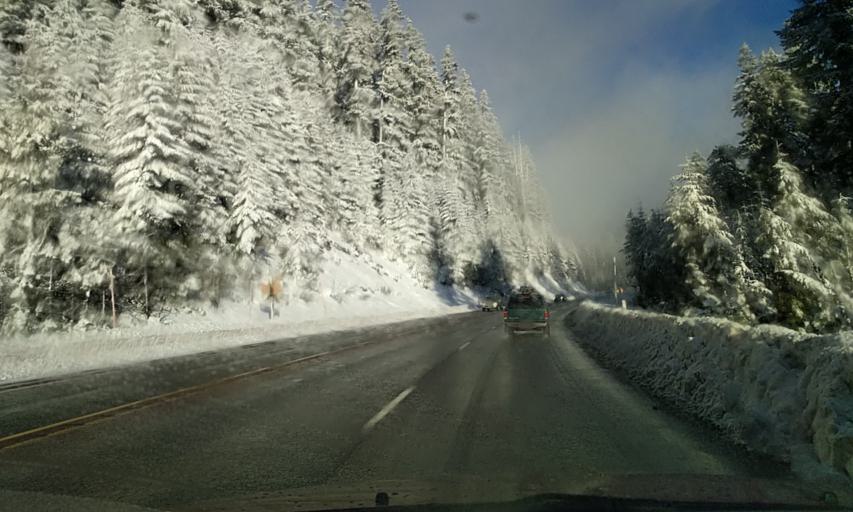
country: US
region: Oregon
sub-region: Clackamas County
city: Mount Hood Village
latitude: 45.2889
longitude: -121.6978
